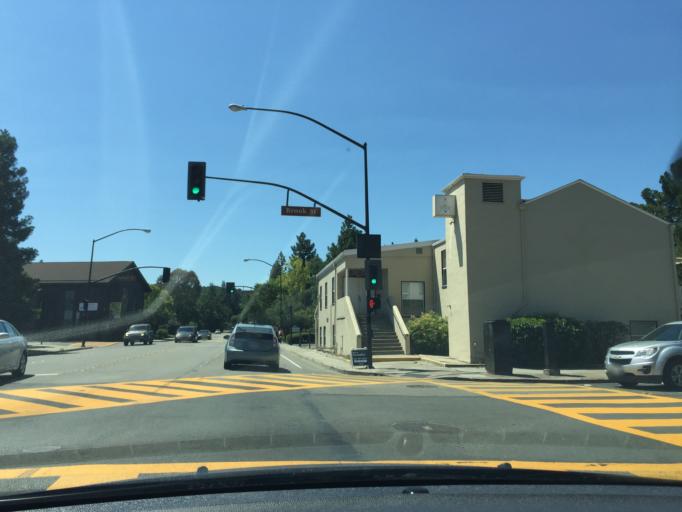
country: US
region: California
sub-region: Contra Costa County
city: Lafayette
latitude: 37.8886
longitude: -122.1183
